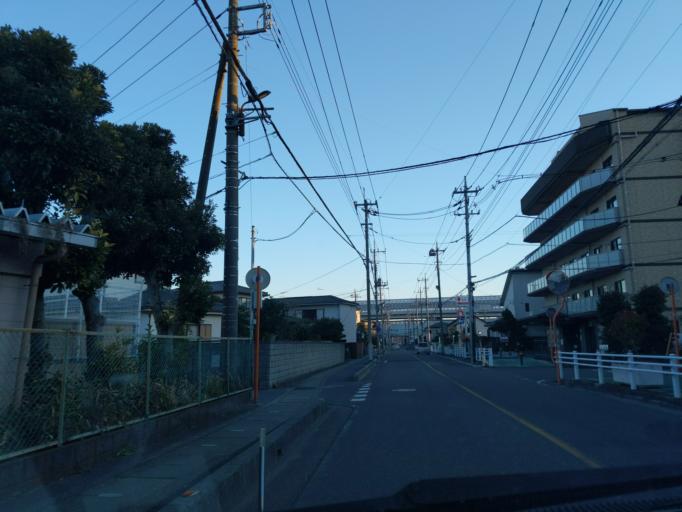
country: JP
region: Saitama
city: Koshigaya
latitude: 35.8509
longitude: 139.7889
